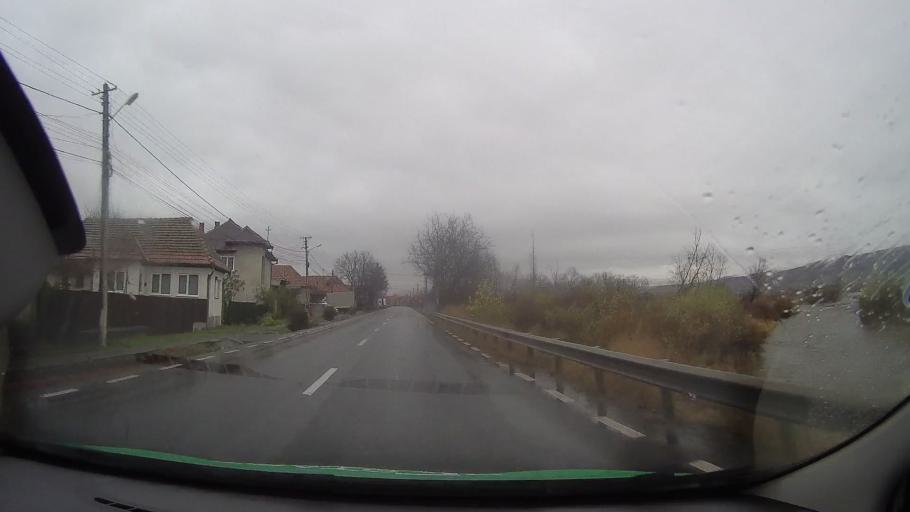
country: RO
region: Mures
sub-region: Comuna Brancovenesti
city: Valenii de Mures
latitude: 46.8871
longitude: 24.7915
